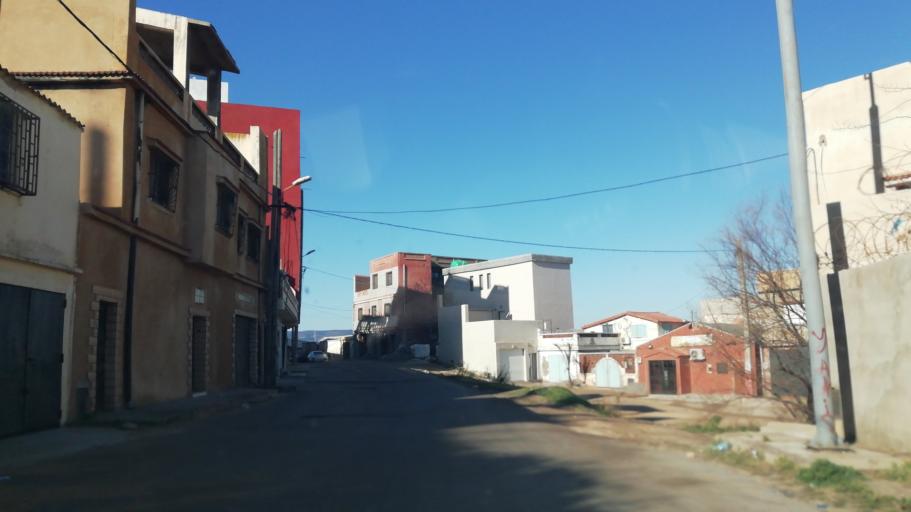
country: DZ
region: Oran
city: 'Ain el Turk
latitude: 35.7274
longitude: -0.8459
